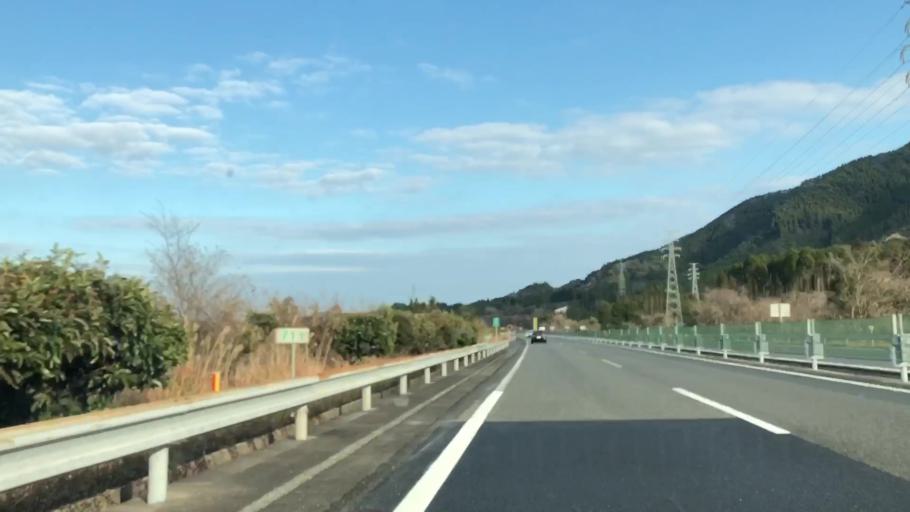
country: JP
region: Miyazaki
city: Miyazaki-shi
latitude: 31.8328
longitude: 131.3324
